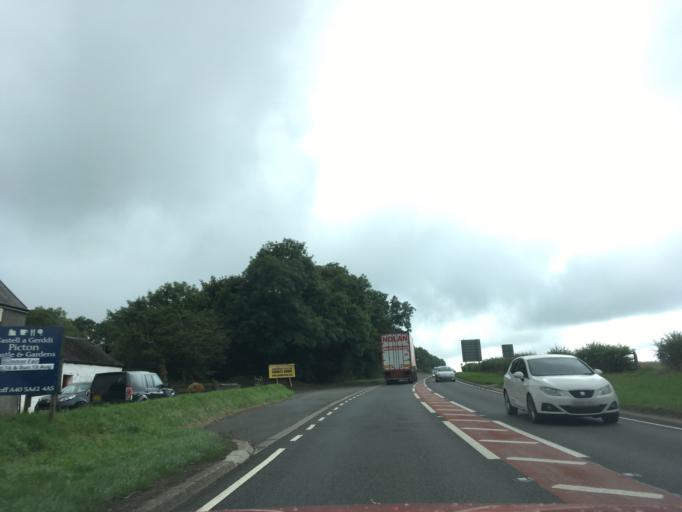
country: GB
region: Wales
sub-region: Pembrokeshire
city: Wiston
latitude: 51.8049
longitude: -4.9086
